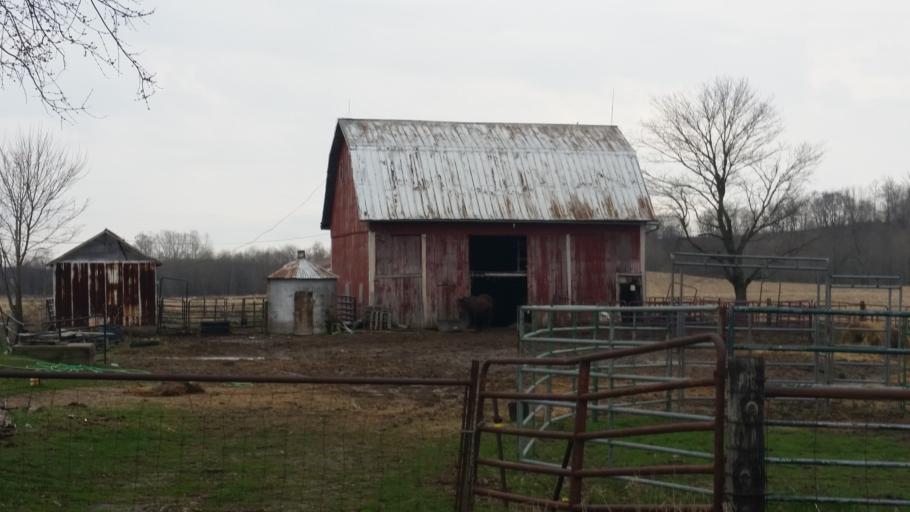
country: US
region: Ohio
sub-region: Knox County
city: Oak Hill
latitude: 40.2936
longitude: -82.2836
